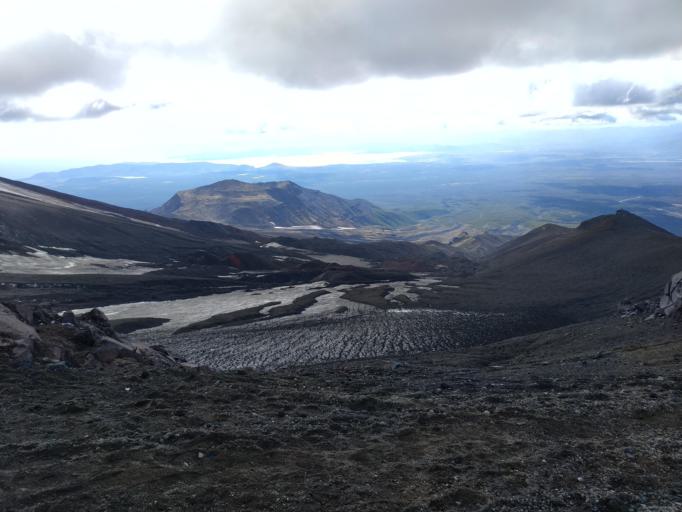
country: RU
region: Kamtsjatka
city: Petropavlovsk-Kamchatsky
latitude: 53.2662
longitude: 158.8116
